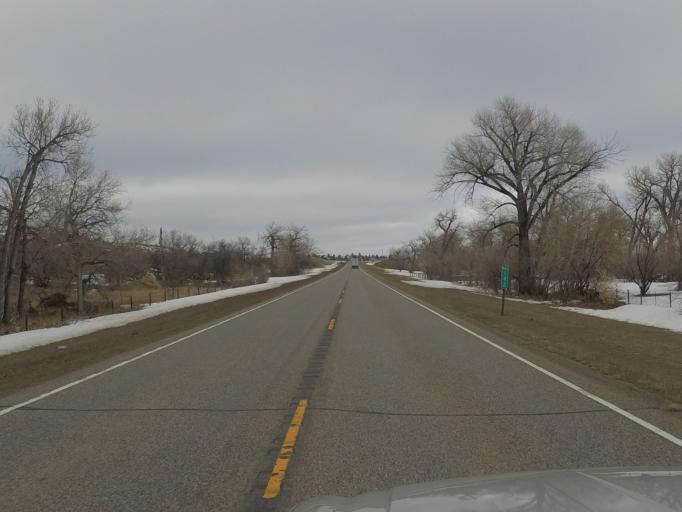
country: US
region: Montana
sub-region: Golden Valley County
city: Ryegate
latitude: 46.3021
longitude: -109.0220
